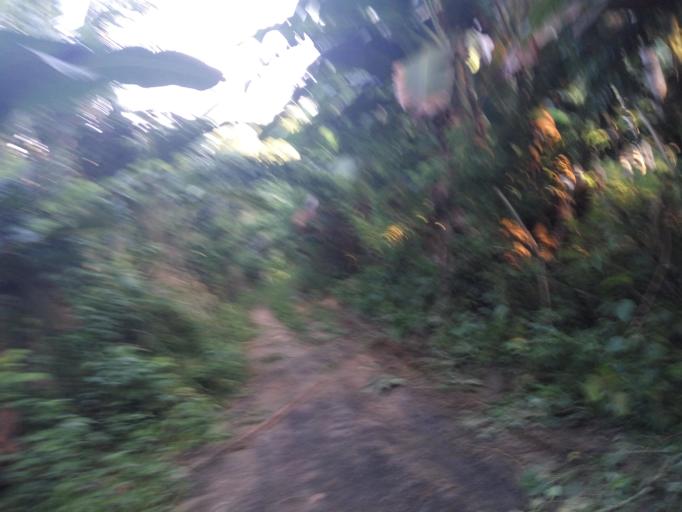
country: PH
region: Central Luzon
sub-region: Province of Aurora
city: Maria Aurora
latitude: 15.8891
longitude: 121.5458
